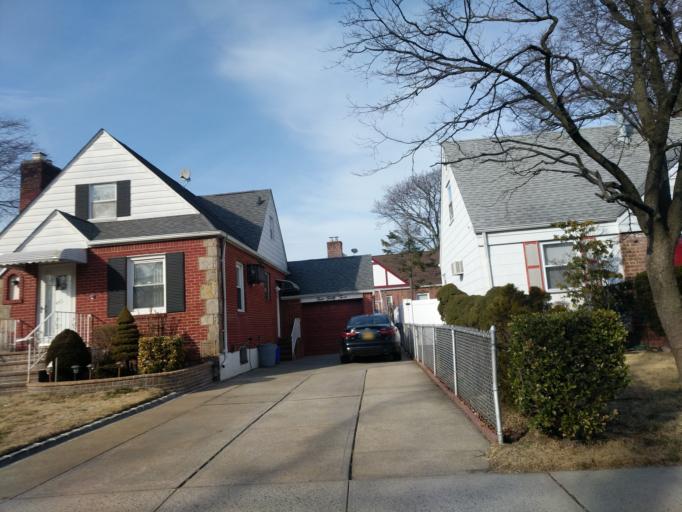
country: US
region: New York
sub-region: Nassau County
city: Valley Stream
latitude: 40.6664
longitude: -73.7161
